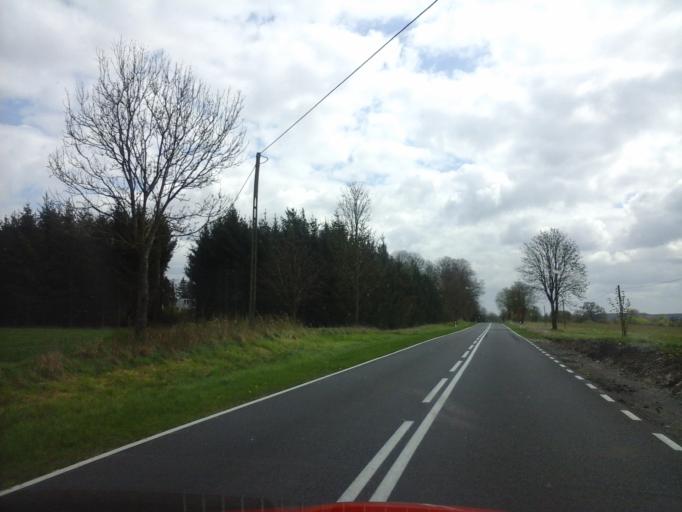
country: PL
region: West Pomeranian Voivodeship
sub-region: Powiat choszczenski
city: Bierzwnik
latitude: 53.0648
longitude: 15.6610
